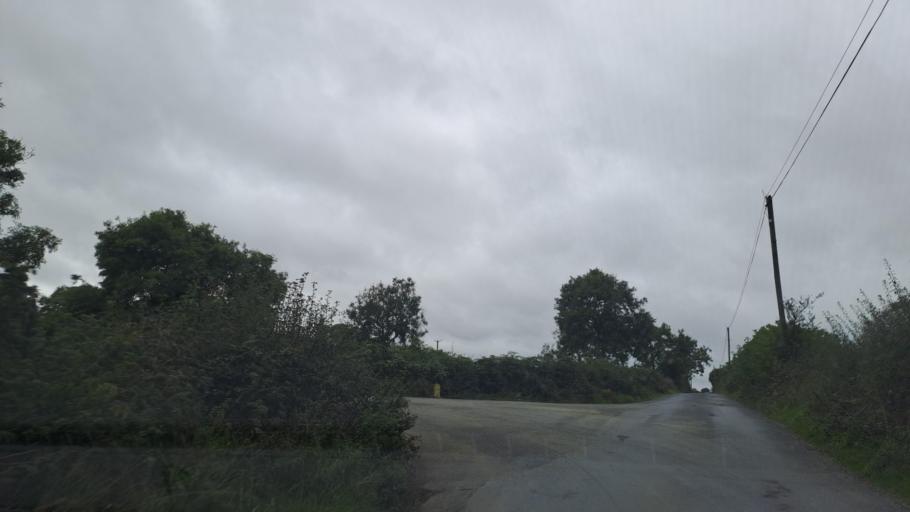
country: IE
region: Ulster
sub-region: An Cabhan
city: Kingscourt
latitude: 54.0026
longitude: -6.8546
